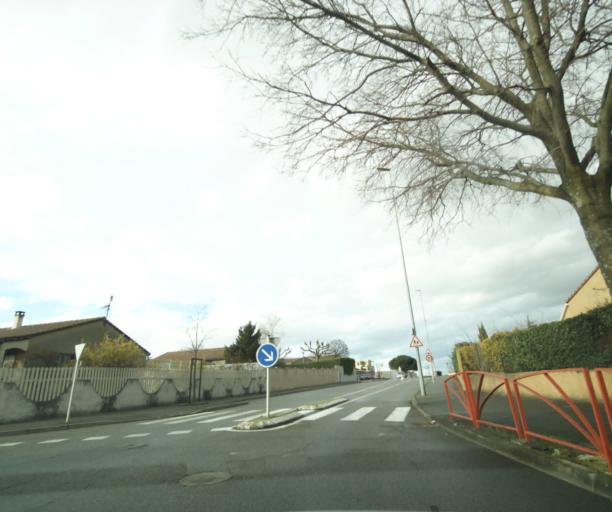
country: FR
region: Rhone-Alpes
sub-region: Departement de la Drome
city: Bourg-les-Valence
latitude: 44.9575
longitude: 4.9064
